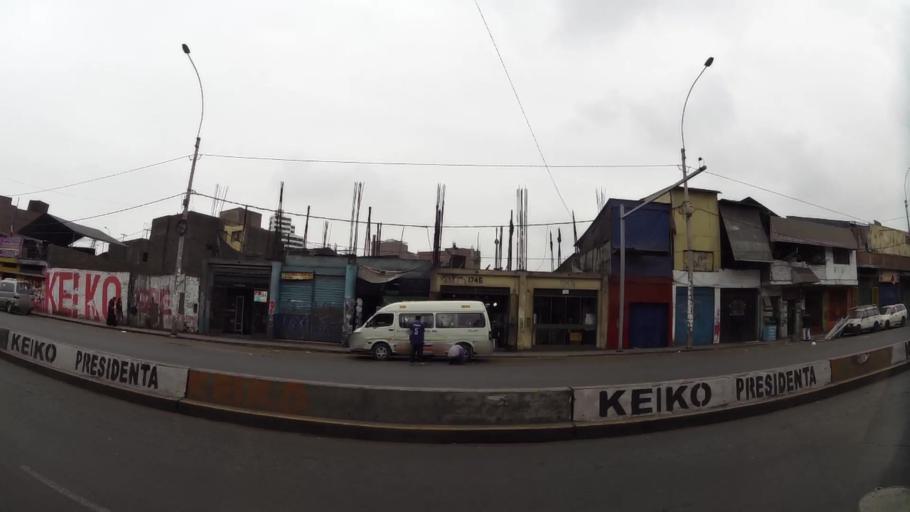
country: PE
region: Lima
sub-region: Lima
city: San Luis
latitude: -12.0713
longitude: -77.0108
